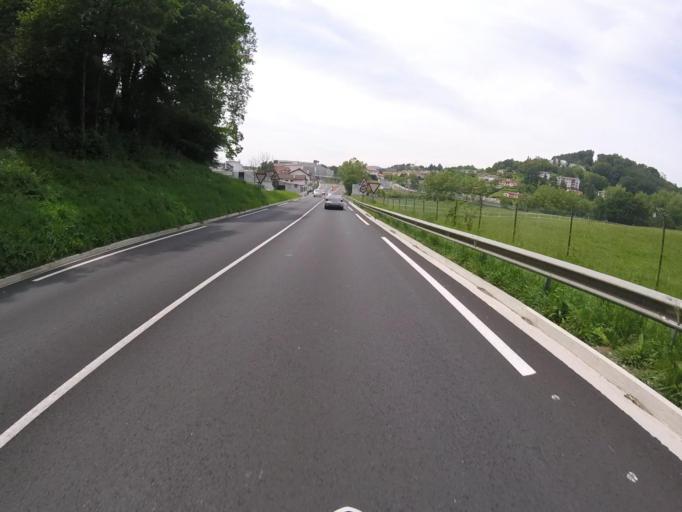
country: ES
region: Basque Country
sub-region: Provincia de Guipuzcoa
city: Lasarte
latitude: 43.2784
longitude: -2.0033
